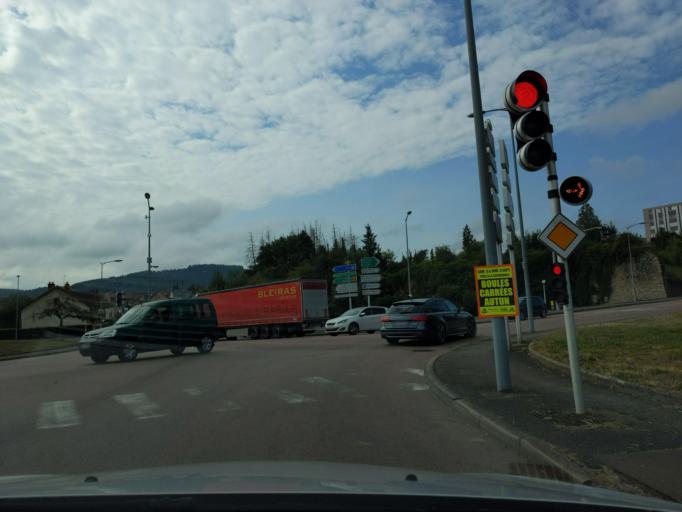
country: FR
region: Bourgogne
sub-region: Departement de Saone-et-Loire
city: Autun
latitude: 46.9603
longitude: 4.3050
